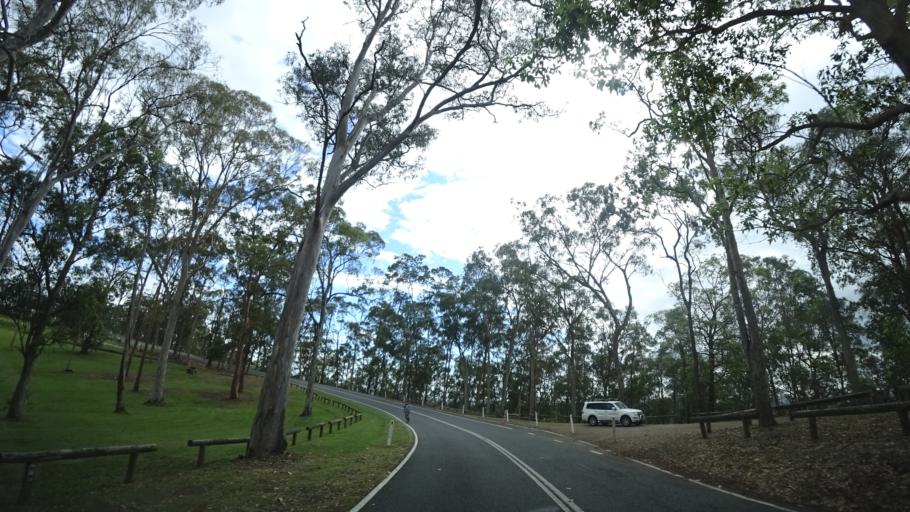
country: AU
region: Queensland
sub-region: Brisbane
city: Kenmore Hills
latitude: -27.4698
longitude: 152.9417
